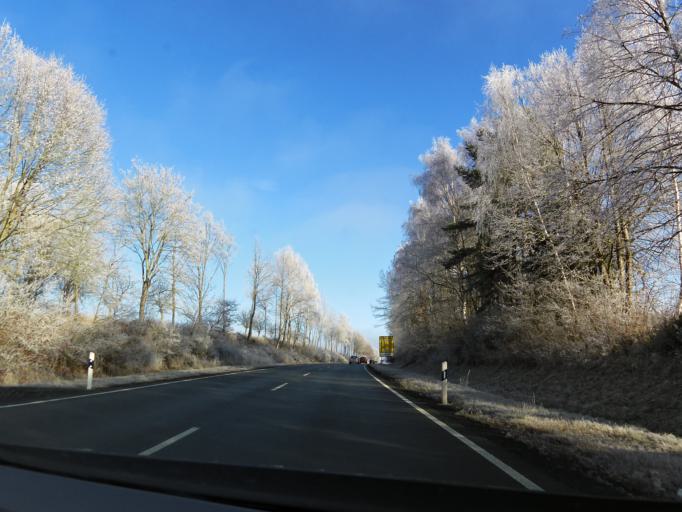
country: DE
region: Bavaria
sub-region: Upper Franconia
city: Arzberg
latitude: 50.0418
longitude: 12.1613
